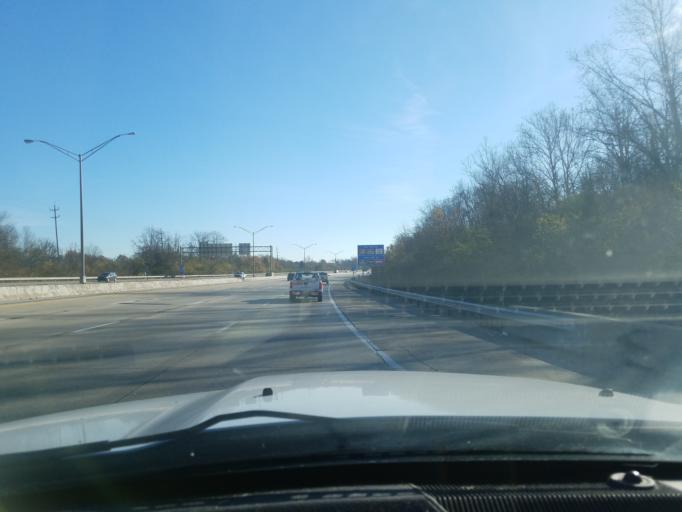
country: US
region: Kentucky
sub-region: Kenton County
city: Crestview Hills
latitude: 39.0316
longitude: -84.5864
